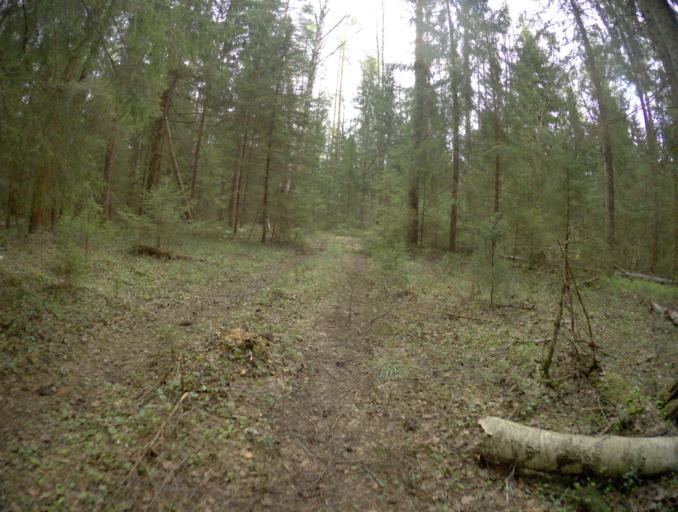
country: RU
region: Vladimir
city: Golovino
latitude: 55.8995
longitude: 40.4693
